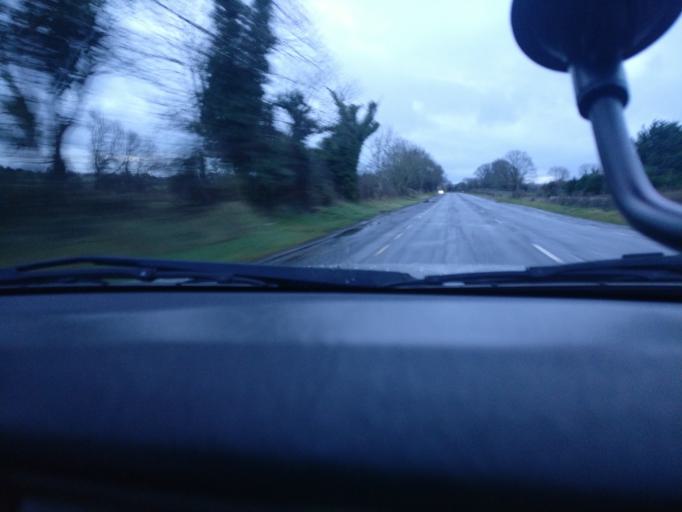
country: IE
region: Connaught
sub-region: County Galway
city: Loughrea
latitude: 53.2409
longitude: -8.4510
